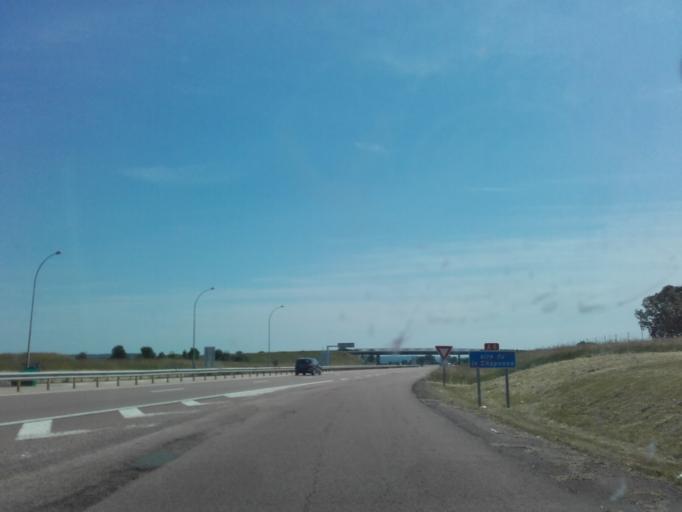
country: FR
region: Bourgogne
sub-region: Departement de l'Yonne
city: Avallon
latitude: 47.5040
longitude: 4.0395
